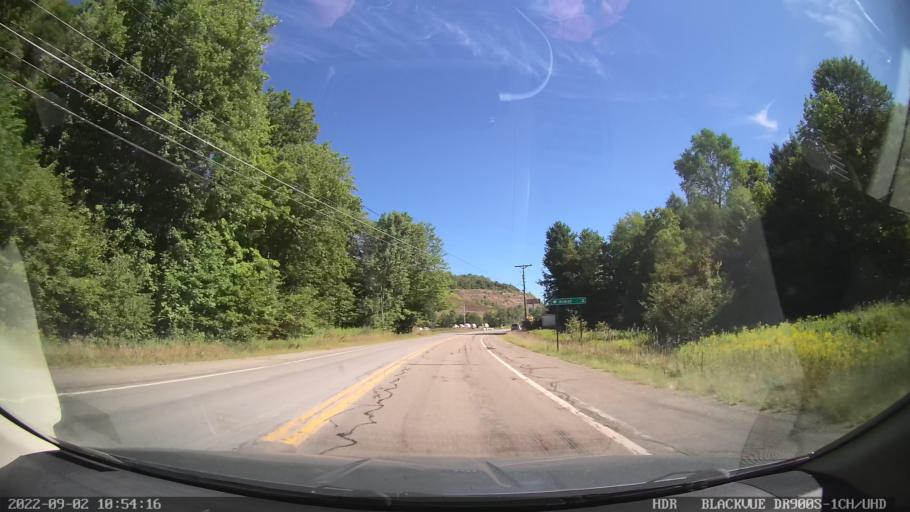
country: US
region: Pennsylvania
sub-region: Tioga County
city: Blossburg
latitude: 41.6572
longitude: -77.0934
